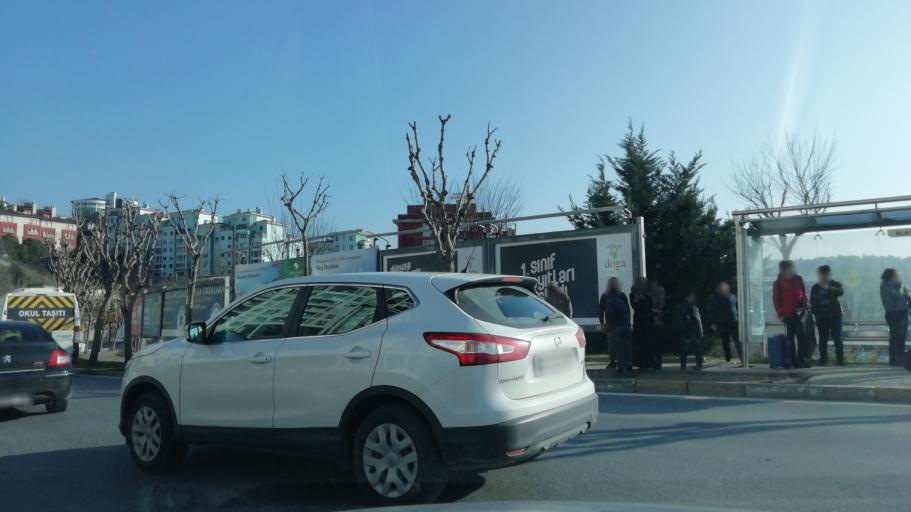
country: TR
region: Istanbul
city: Esenyurt
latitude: 41.0730
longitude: 28.6923
